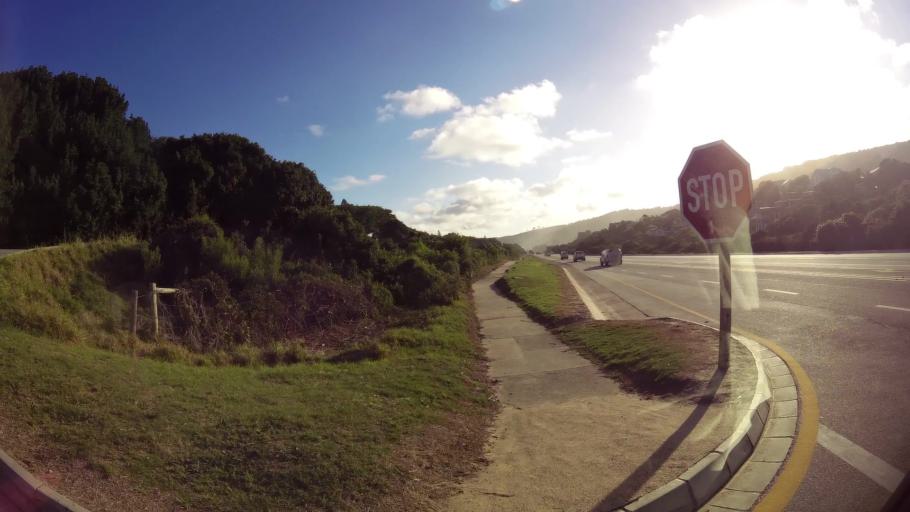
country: ZA
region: Western Cape
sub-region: Eden District Municipality
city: George
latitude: -33.9952
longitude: 22.5900
